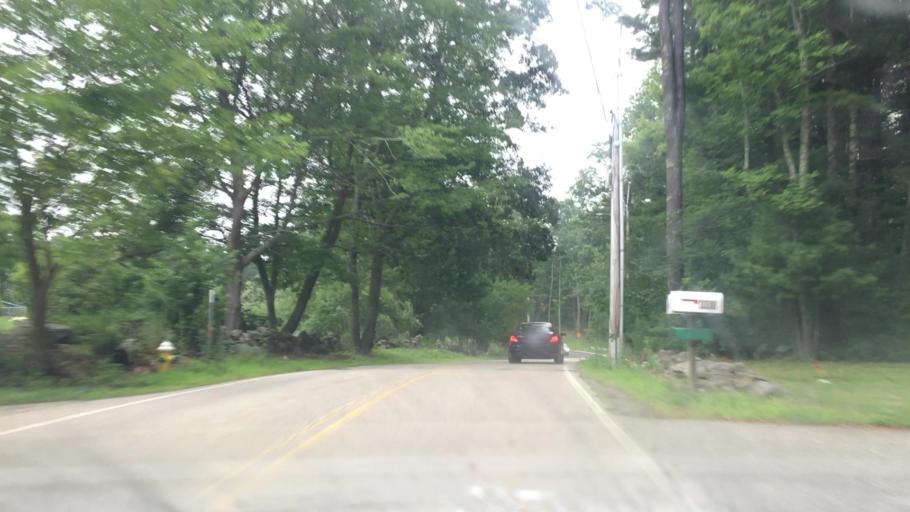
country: US
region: New Hampshire
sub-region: Rockingham County
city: Greenland
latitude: 43.0977
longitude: -70.8395
